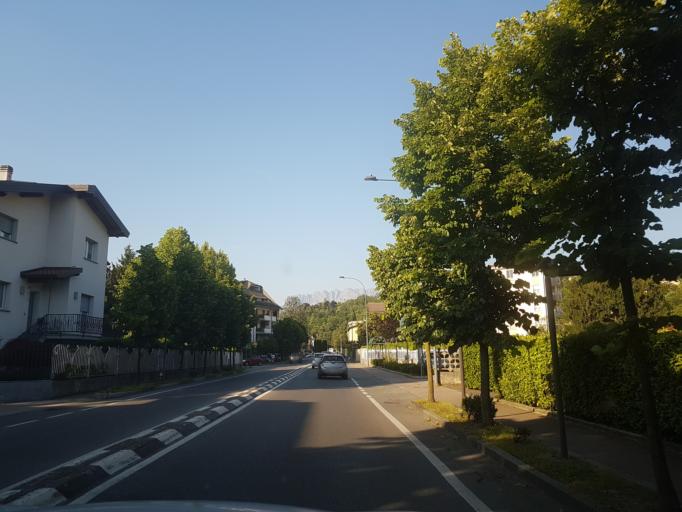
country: IT
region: Lombardy
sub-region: Provincia di Lecco
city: Oggiono
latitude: 45.7875
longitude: 9.3471
